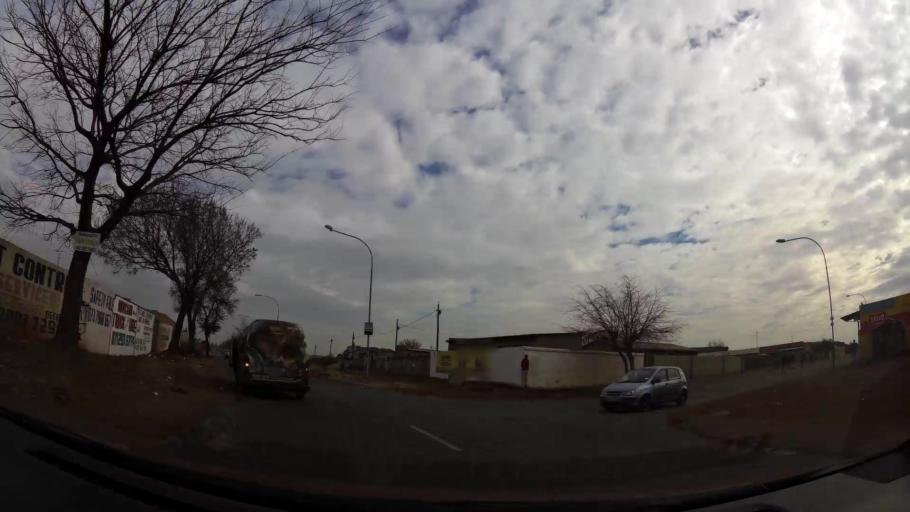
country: ZA
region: Gauteng
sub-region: City of Johannesburg Metropolitan Municipality
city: Soweto
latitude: -26.2728
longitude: 27.8420
